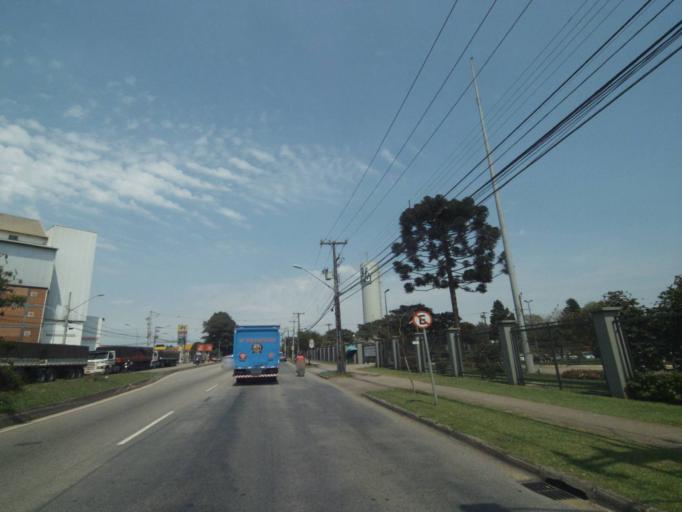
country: BR
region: Parana
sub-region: Curitiba
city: Curitiba
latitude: -25.4861
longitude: -49.3187
